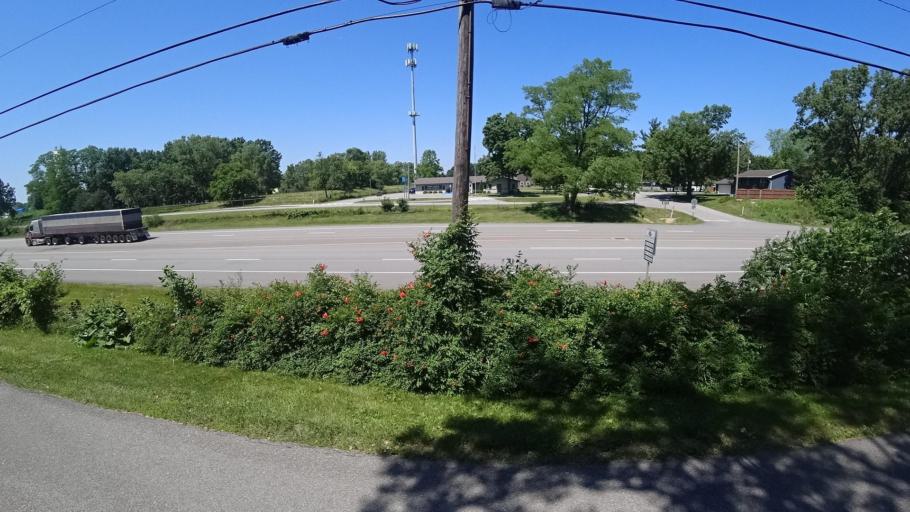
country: US
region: Indiana
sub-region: Porter County
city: Burns Harbor
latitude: 41.6124
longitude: -87.1254
